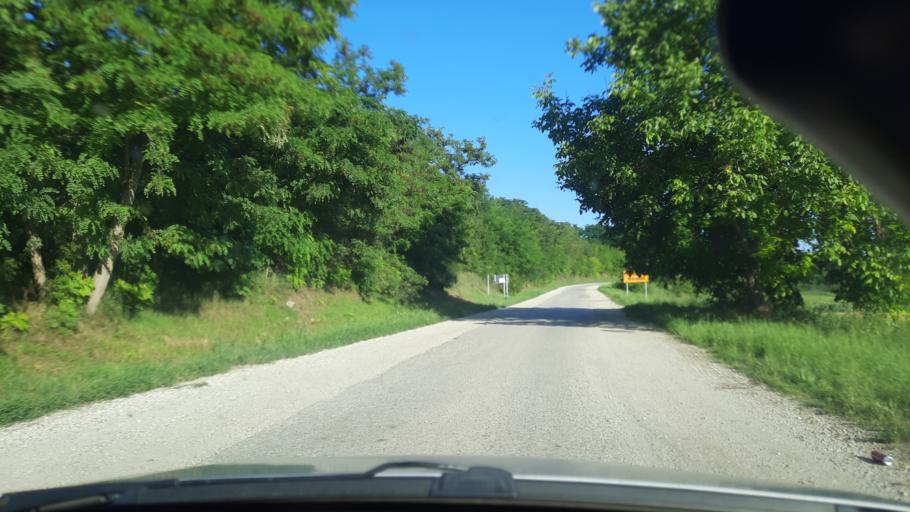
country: RS
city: Cortanovci
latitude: 45.1042
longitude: 19.9882
